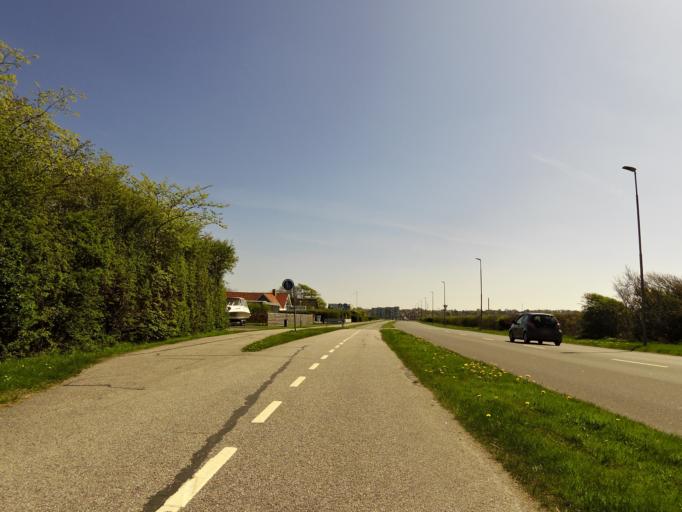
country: DK
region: Central Jutland
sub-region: Struer Kommune
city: Struer
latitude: 56.5020
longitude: 8.5820
